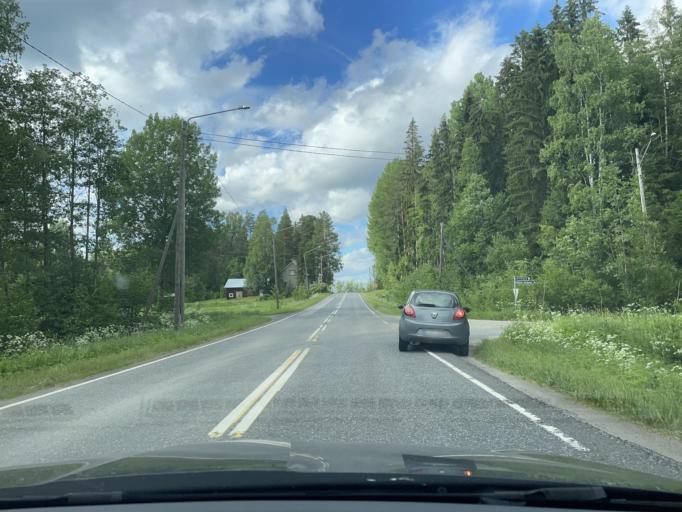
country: FI
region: Central Finland
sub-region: Jaemsae
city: Jaemsaenkoski
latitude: 61.9695
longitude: 25.1619
